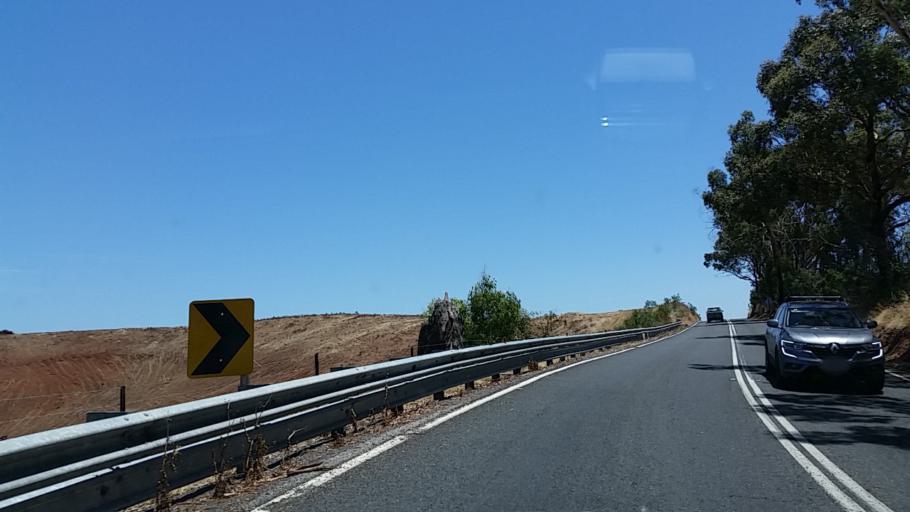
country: AU
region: South Australia
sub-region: Adelaide Hills
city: Gumeracha
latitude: -34.8244
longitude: 138.8427
